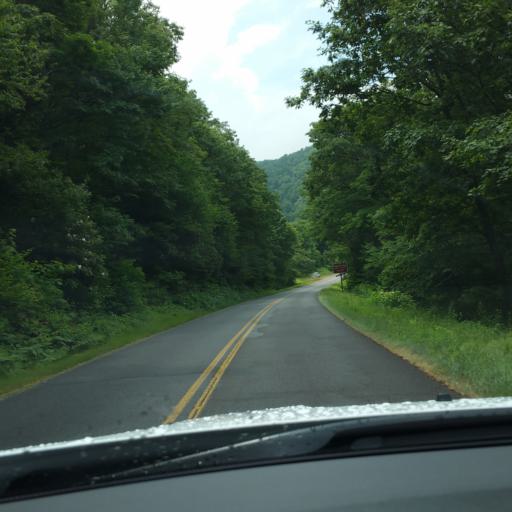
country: US
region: North Carolina
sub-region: Transylvania County
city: Brevard
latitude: 35.3676
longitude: -82.7926
